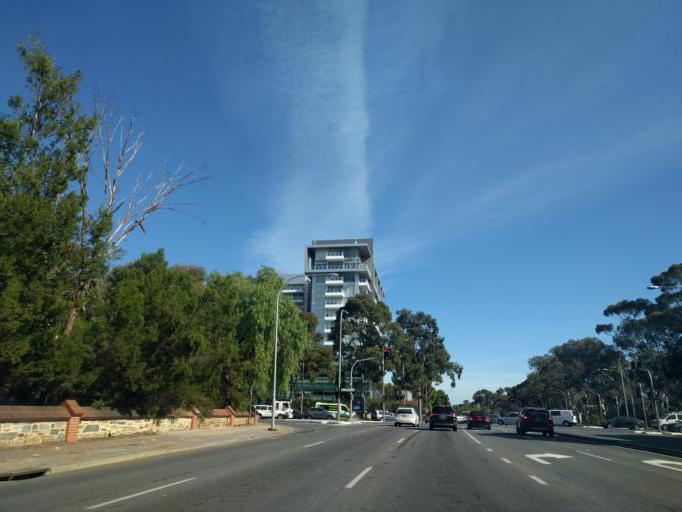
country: AU
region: South Australia
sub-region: Unley
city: Fullarton
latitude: -34.9402
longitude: 138.6253
